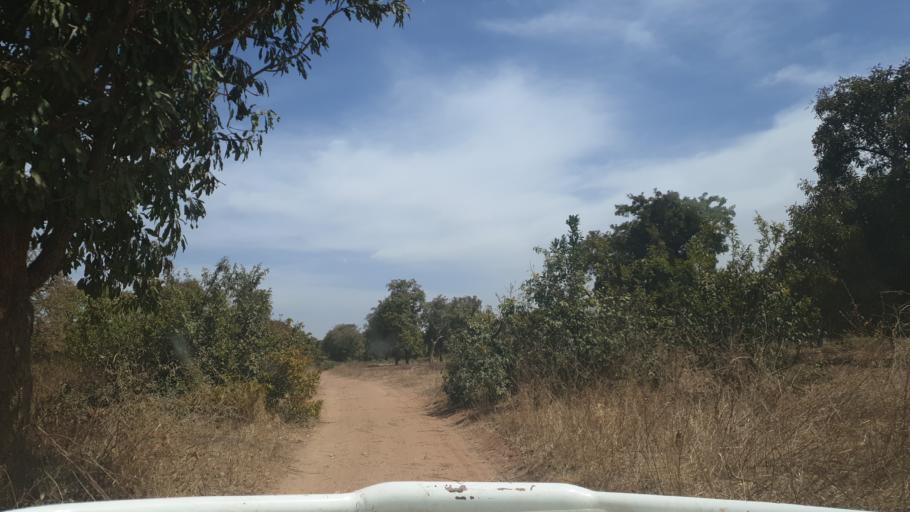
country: ML
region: Sikasso
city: Yorosso
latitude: 12.2886
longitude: -4.6712
